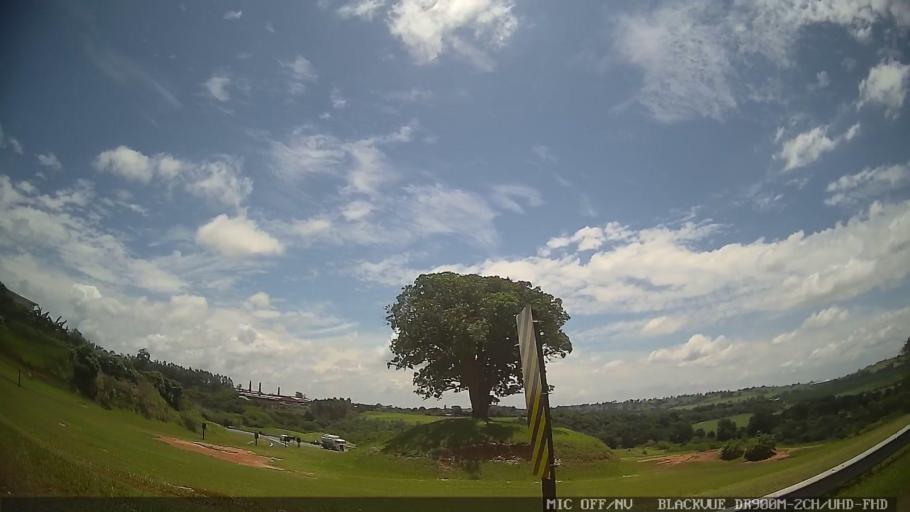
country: BR
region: Sao Paulo
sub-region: Laranjal Paulista
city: Laranjal Paulista
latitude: -23.0444
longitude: -47.8277
